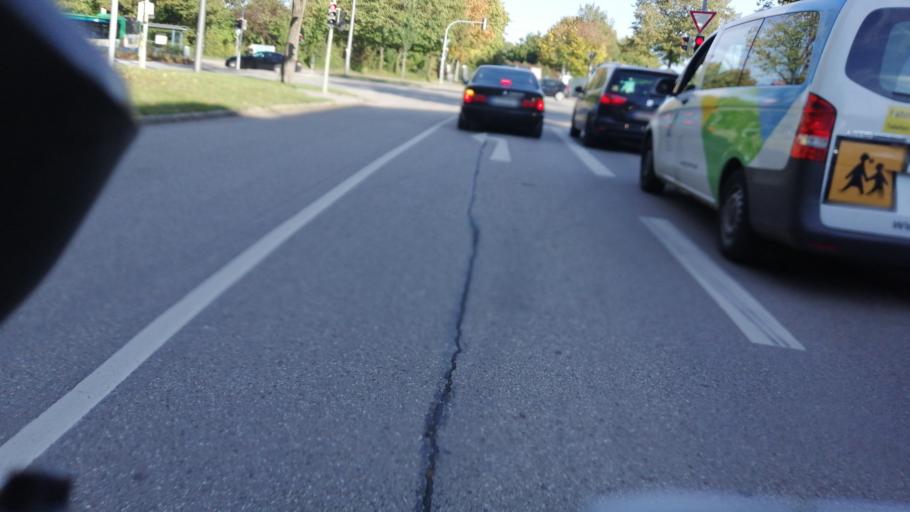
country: DE
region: Bavaria
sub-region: Upper Bavaria
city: Oberschleissheim
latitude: 48.2057
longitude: 11.5857
